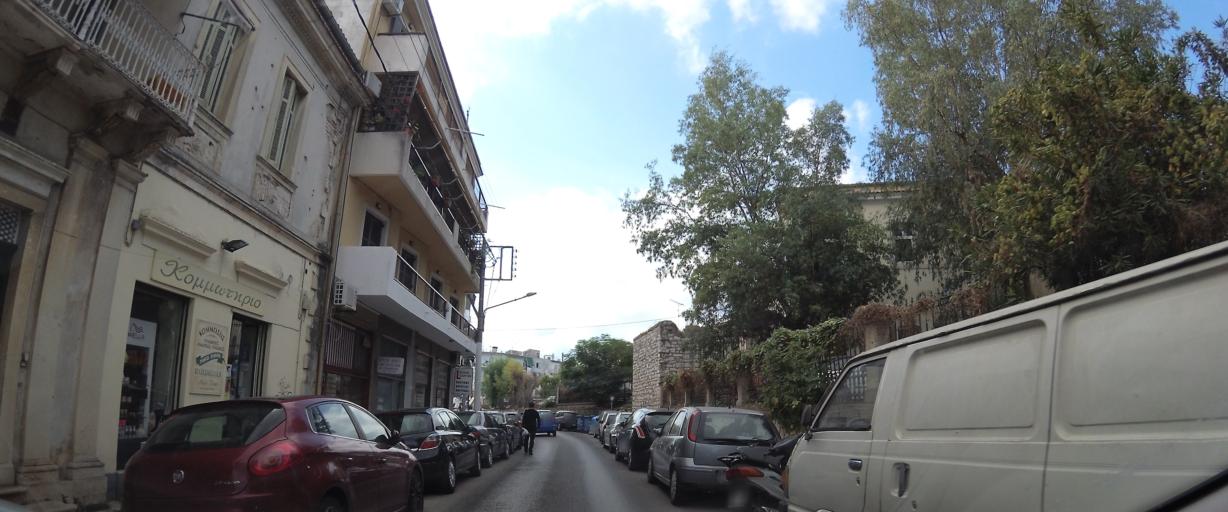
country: GR
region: Ionian Islands
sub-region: Nomos Kerkyras
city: Kerkyra
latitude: 39.6207
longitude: 19.9160
